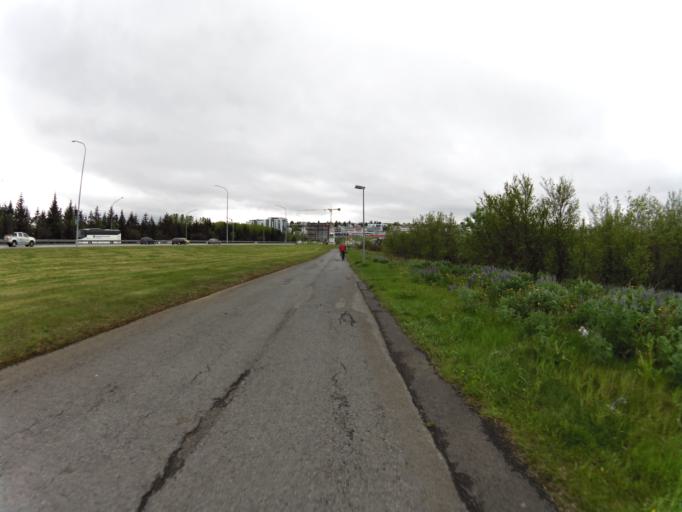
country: IS
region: Capital Region
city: Kopavogur
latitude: 64.1196
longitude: -21.8996
